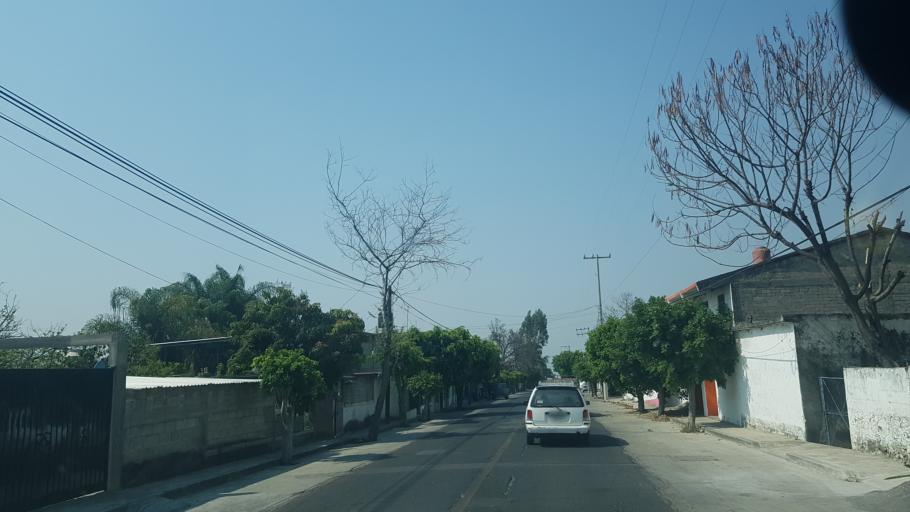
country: MX
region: Morelos
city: Tlacotepec
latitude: 18.8099
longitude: -98.7583
